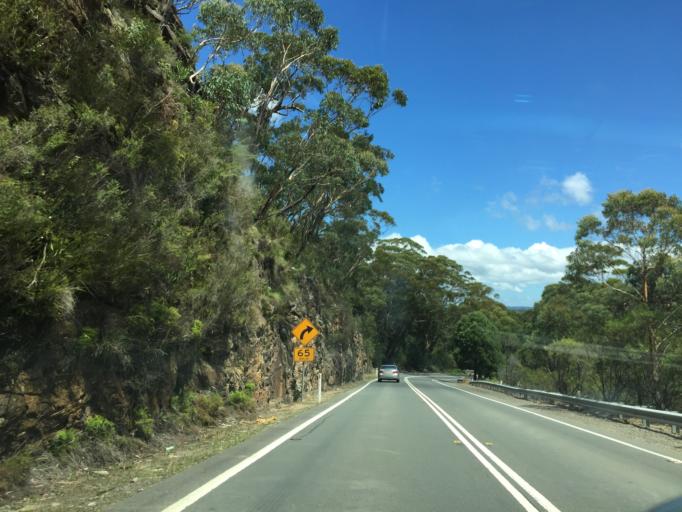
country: AU
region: New South Wales
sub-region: Blue Mountains Municipality
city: Blackheath
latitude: -33.5488
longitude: 150.4002
